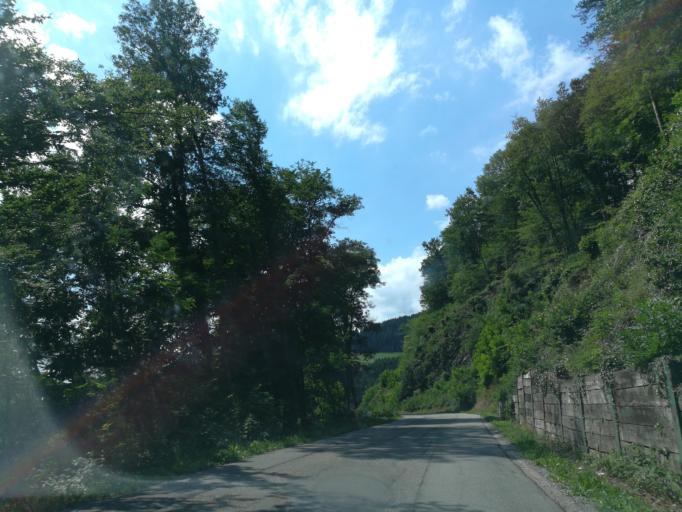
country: DE
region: Baden-Wuerttemberg
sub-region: Freiburg Region
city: Hausach
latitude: 48.2883
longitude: 8.1911
